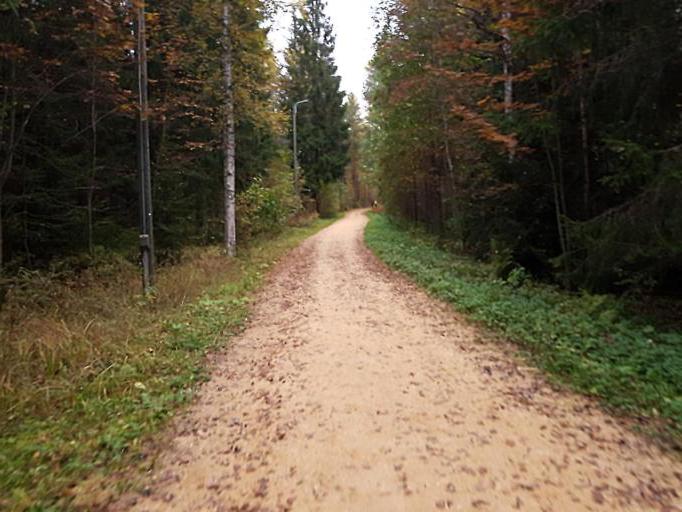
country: FI
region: Uusimaa
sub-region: Helsinki
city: Helsinki
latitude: 60.2573
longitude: 24.9064
